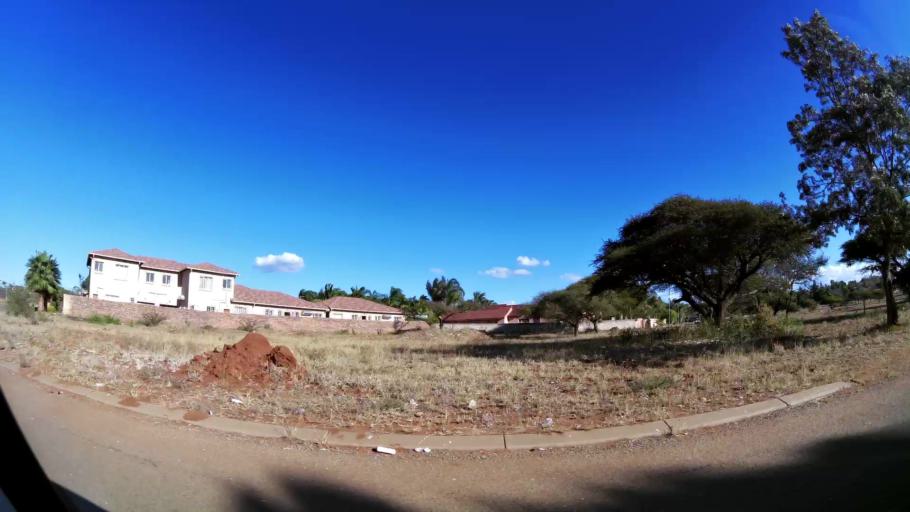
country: ZA
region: Limpopo
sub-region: Capricorn District Municipality
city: Polokwane
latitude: -23.8829
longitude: 29.4934
